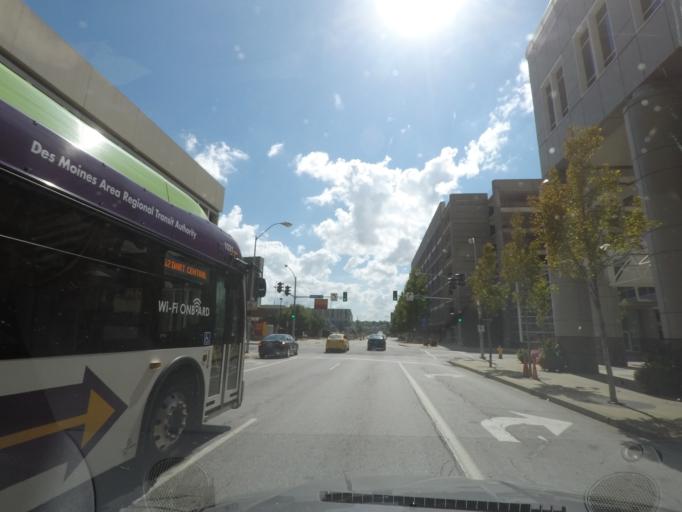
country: US
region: Iowa
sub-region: Polk County
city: Des Moines
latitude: 41.5854
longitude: -93.6258
